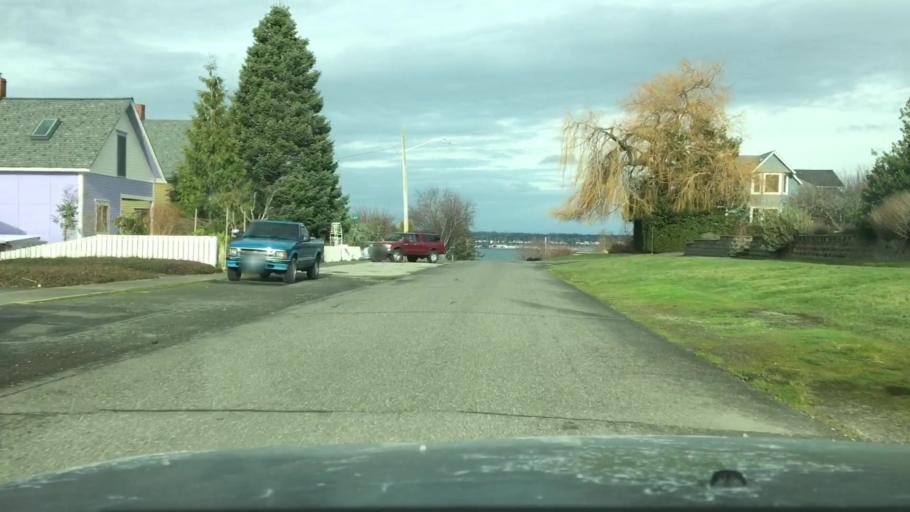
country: US
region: Washington
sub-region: Whatcom County
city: Bellingham
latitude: 48.7279
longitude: -122.5015
